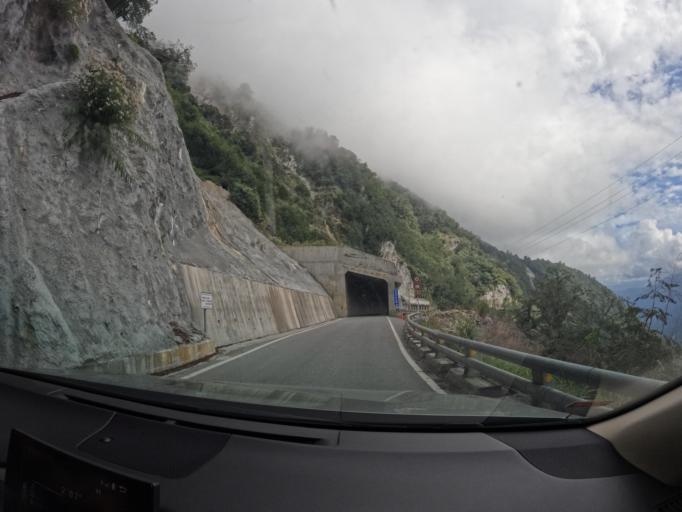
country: TW
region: Taiwan
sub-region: Taitung
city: Taitung
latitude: 23.2404
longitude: 121.0021
